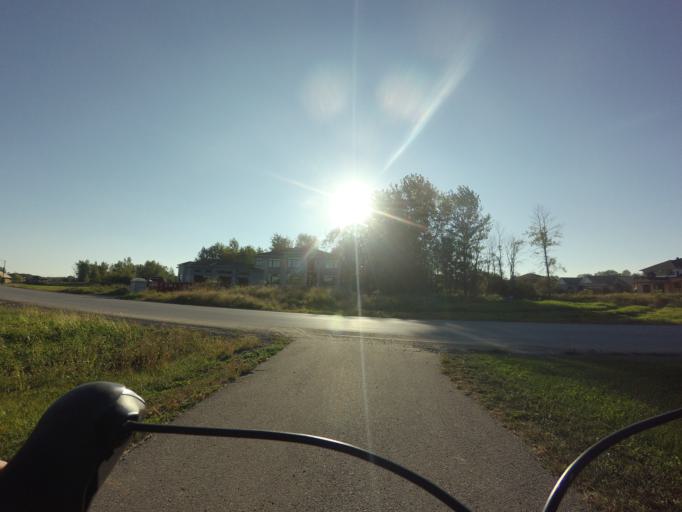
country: CA
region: Ontario
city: Bells Corners
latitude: 45.2145
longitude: -75.7031
